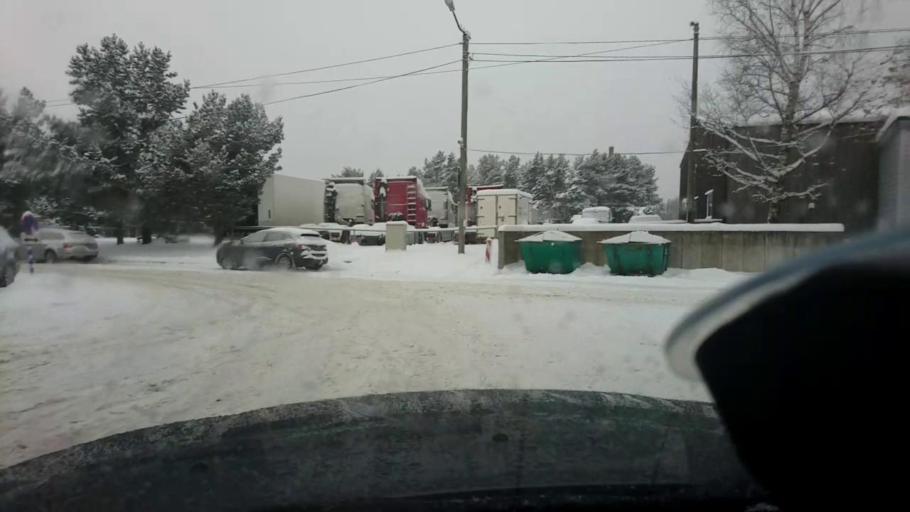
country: EE
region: Harju
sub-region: Saue vald
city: Laagri
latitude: 59.3583
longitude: 24.6341
